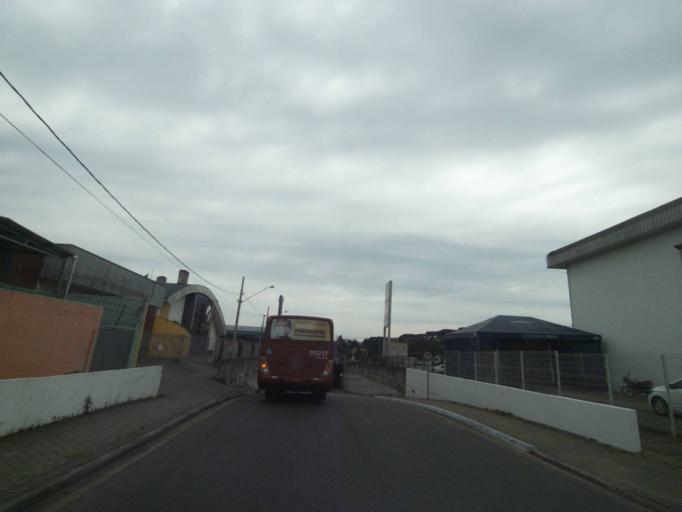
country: BR
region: Parana
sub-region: Sao Jose Dos Pinhais
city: Sao Jose dos Pinhais
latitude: -25.5182
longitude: -49.2009
